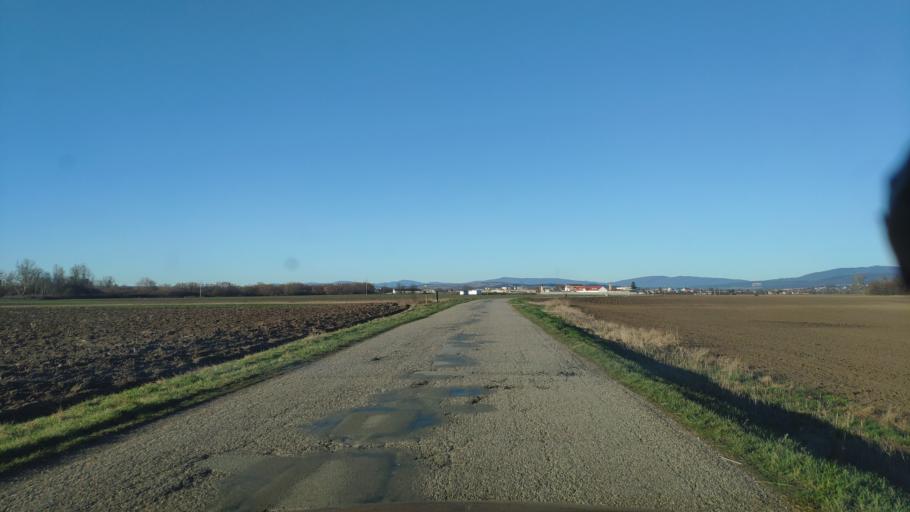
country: HU
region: Borsod-Abauj-Zemplen
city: Gonc
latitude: 48.5930
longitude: 21.3136
